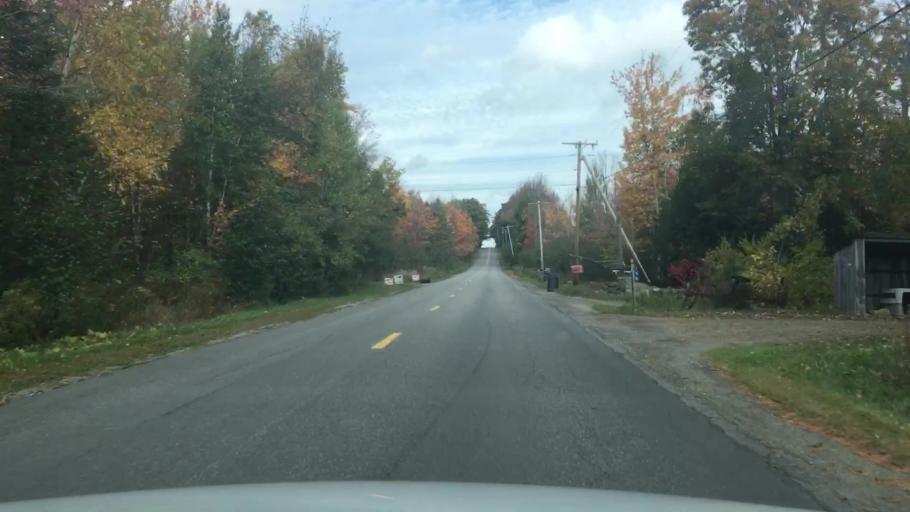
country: US
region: Maine
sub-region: Waldo County
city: Searsmont
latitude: 44.3873
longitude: -69.1330
